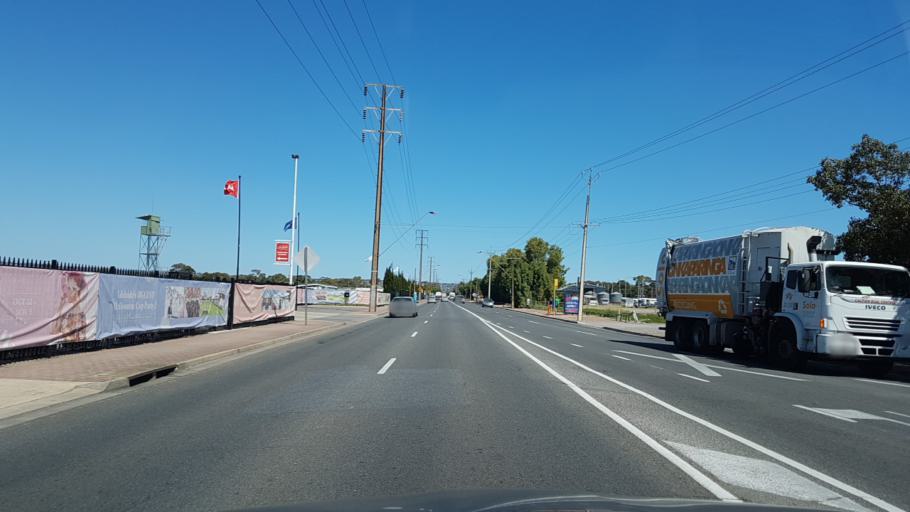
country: AU
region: South Australia
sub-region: Holdfast Bay
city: Glenelg East
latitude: -34.9768
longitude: 138.5379
